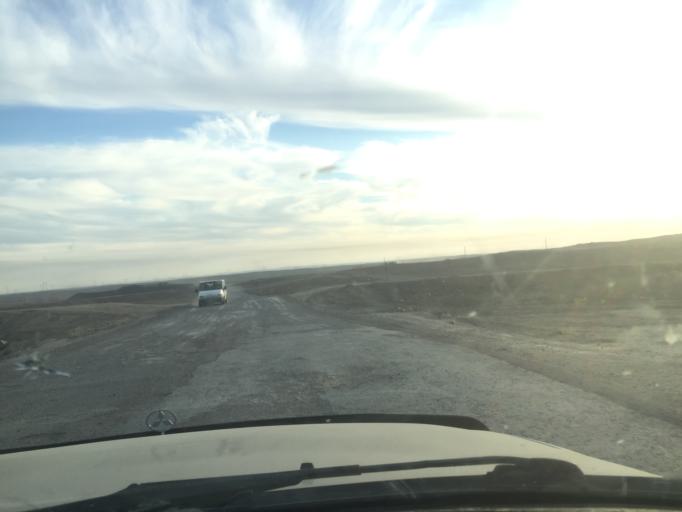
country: KZ
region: Almaty Oblysy
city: Ulken
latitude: 45.1571
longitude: 73.9464
